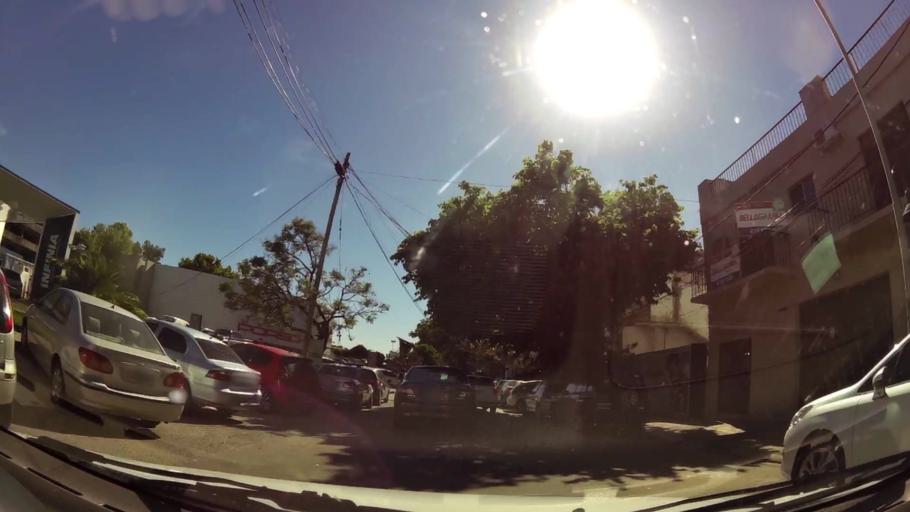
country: AR
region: Buenos Aires
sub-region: Partido de Vicente Lopez
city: Olivos
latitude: -34.5256
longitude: -58.4714
